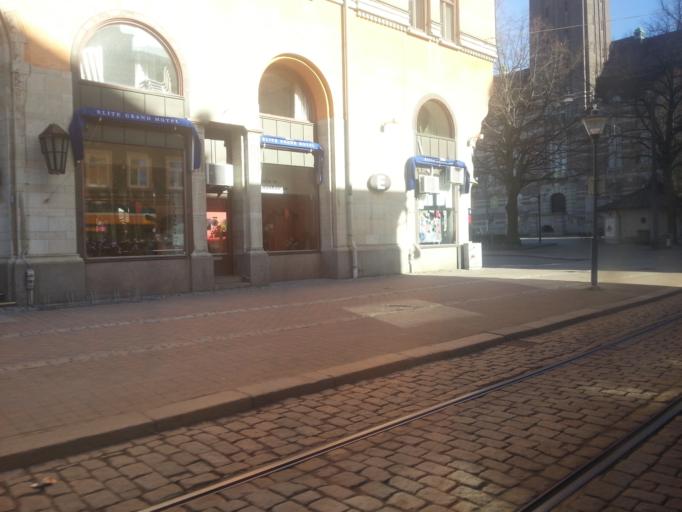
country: SE
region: OEstergoetland
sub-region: Norrkopings Kommun
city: Norrkoping
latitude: 58.5930
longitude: 16.1859
